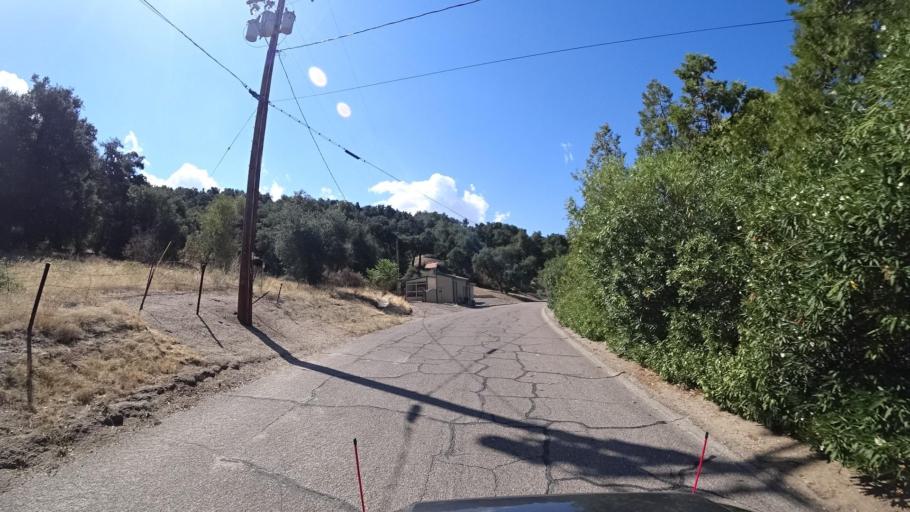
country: US
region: California
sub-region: San Diego County
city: Julian
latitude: 33.2853
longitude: -116.6150
